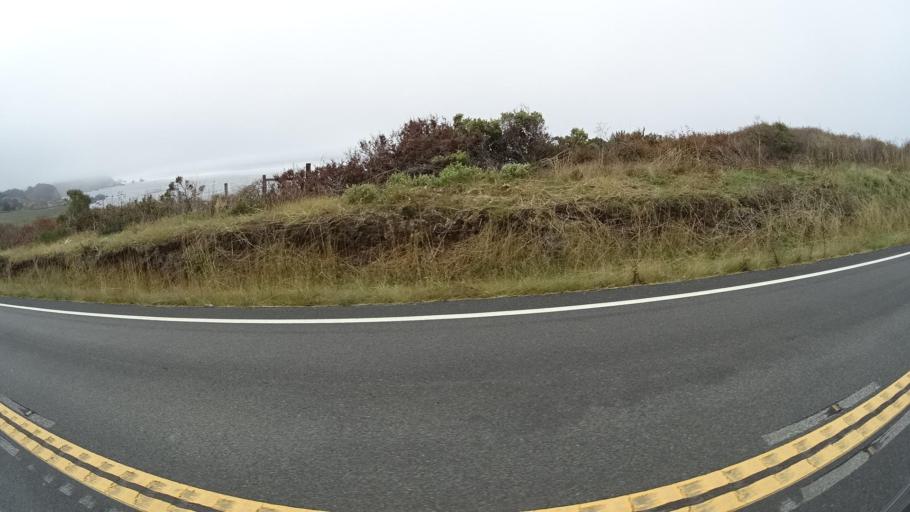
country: US
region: California
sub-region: Monterey County
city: Carmel-by-the-Sea
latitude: 36.3995
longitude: -121.9056
